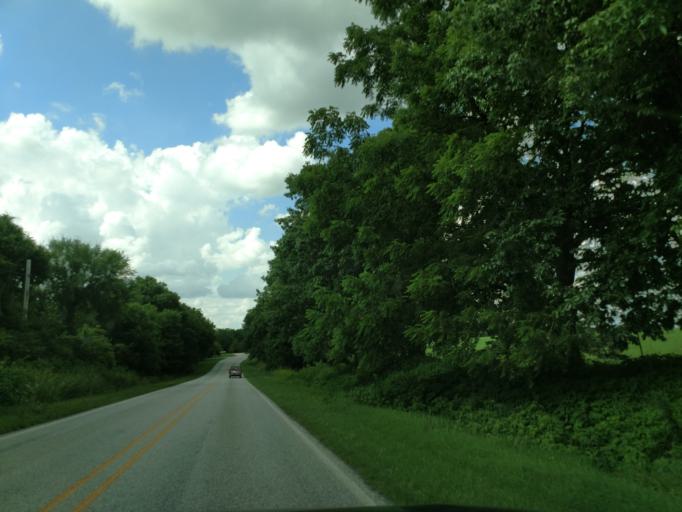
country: US
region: Arkansas
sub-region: Carroll County
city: Berryville
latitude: 36.4039
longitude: -93.5660
